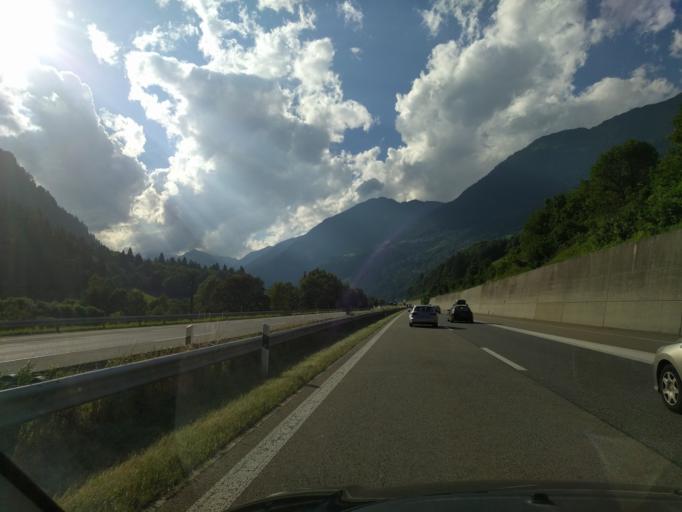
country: CH
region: Ticino
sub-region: Leventina District
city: Faido
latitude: 46.5021
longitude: 8.7237
